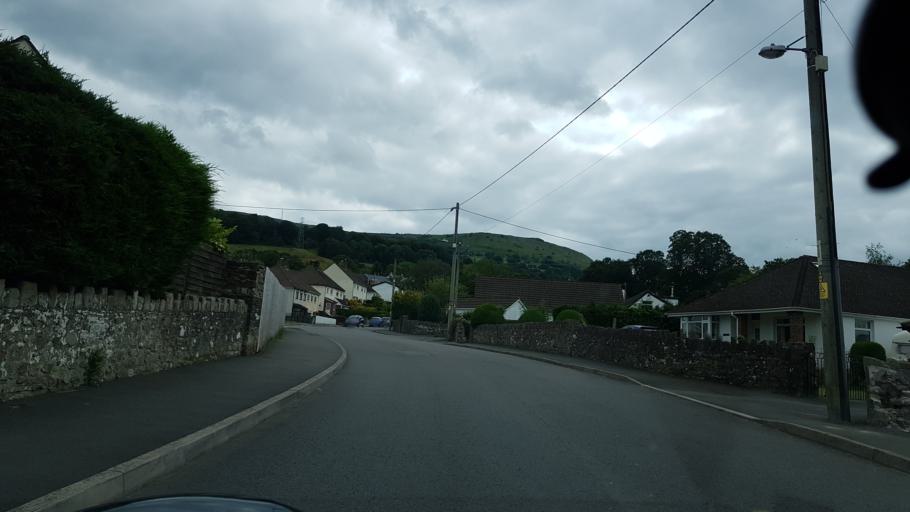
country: GB
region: Wales
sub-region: Monmouthshire
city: Gilwern
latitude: 51.8276
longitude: -3.0935
